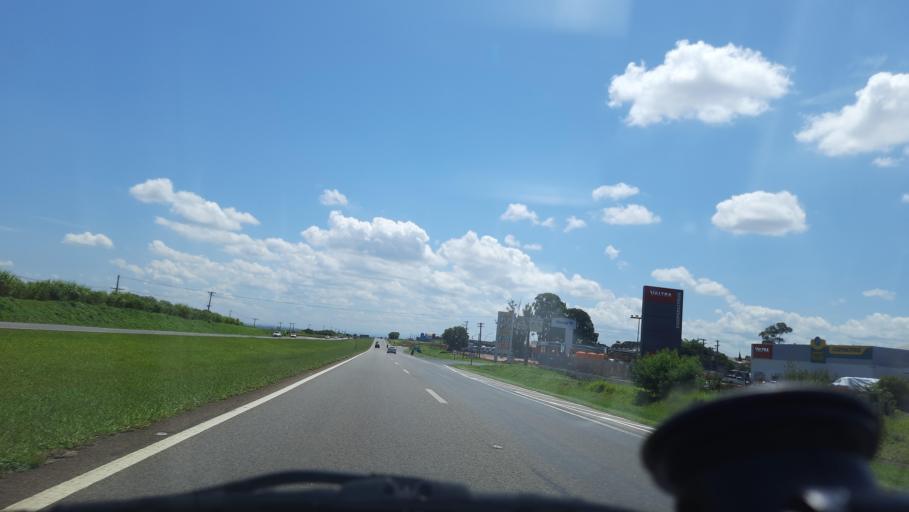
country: BR
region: Sao Paulo
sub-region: Mogi-Mirim
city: Mogi Mirim
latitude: -22.4200
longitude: -46.9799
